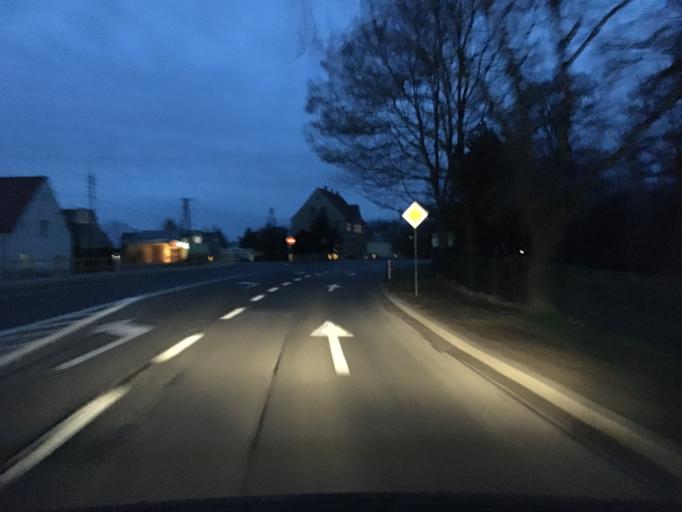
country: PL
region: Opole Voivodeship
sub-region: Powiat brzeski
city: Losiow
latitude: 50.7921
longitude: 17.5563
